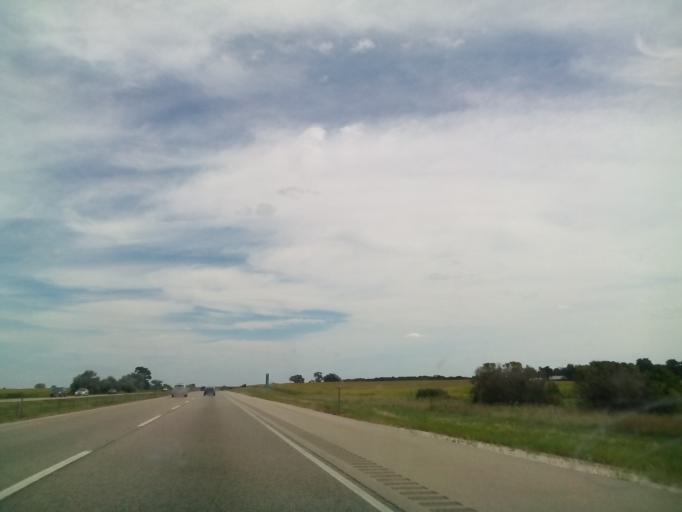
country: US
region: Illinois
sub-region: Kane County
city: Maple Park
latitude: 41.8674
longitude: -88.5759
